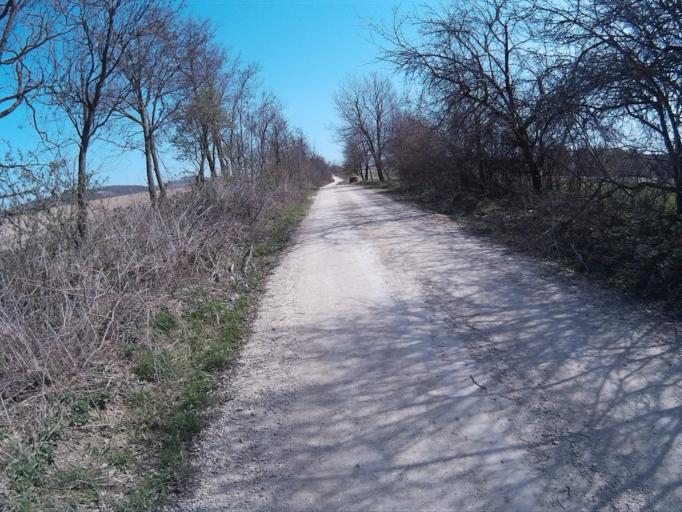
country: HU
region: Veszprem
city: Herend
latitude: 47.1997
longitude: 17.7876
